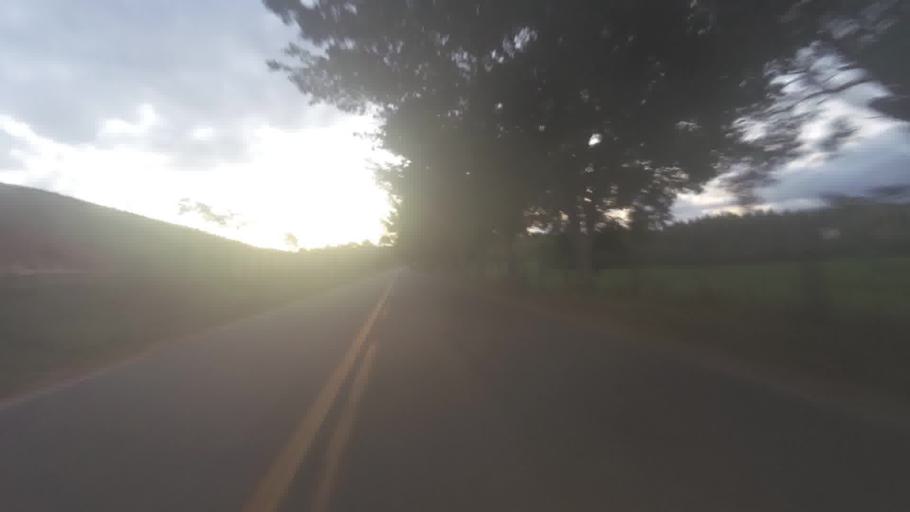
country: BR
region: Espirito Santo
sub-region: Itapemirim
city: Itapemirim
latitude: -20.9539
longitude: -40.8764
